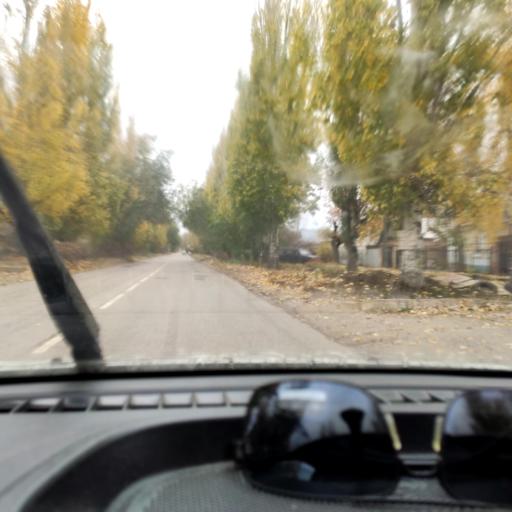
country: RU
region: Samara
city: Tol'yatti
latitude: 53.5341
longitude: 49.4178
